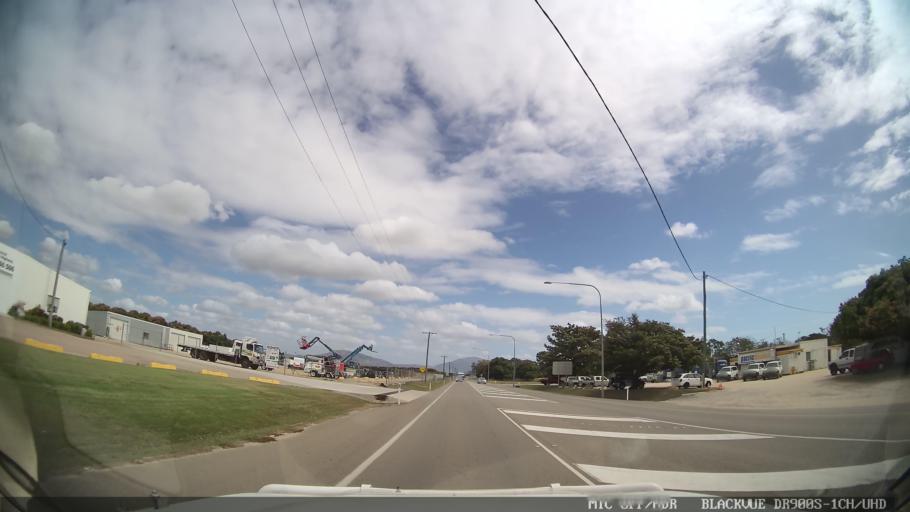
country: AU
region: Queensland
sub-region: Whitsunday
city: Bowen
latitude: -20.0163
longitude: 148.1897
